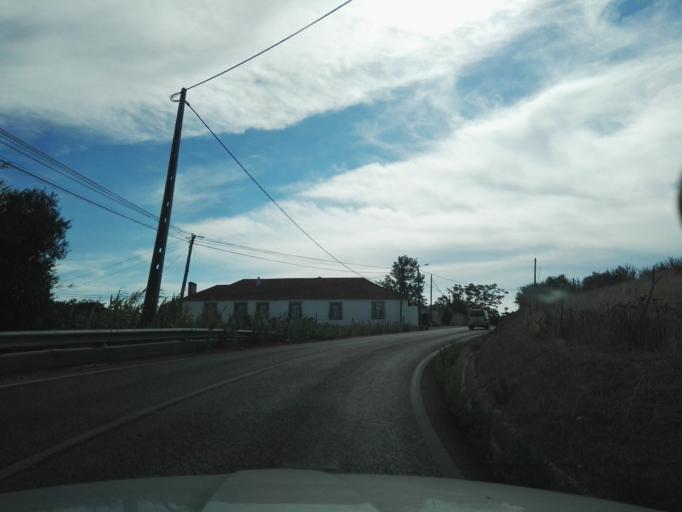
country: PT
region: Lisbon
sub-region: Arruda Dos Vinhos
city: Arruda dos Vinhos
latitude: 38.9750
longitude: -9.0519
